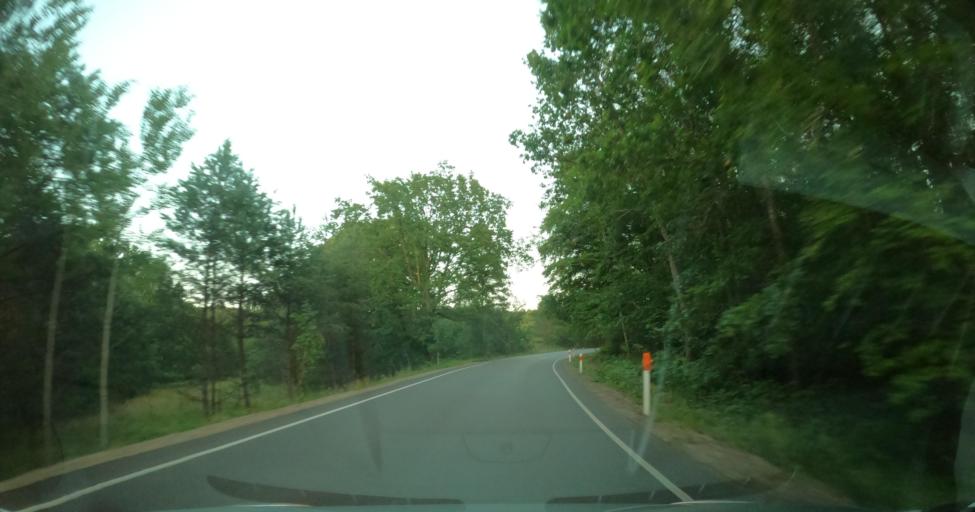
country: PL
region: Pomeranian Voivodeship
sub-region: Powiat leborski
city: Lebork
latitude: 54.5168
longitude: 17.7971
